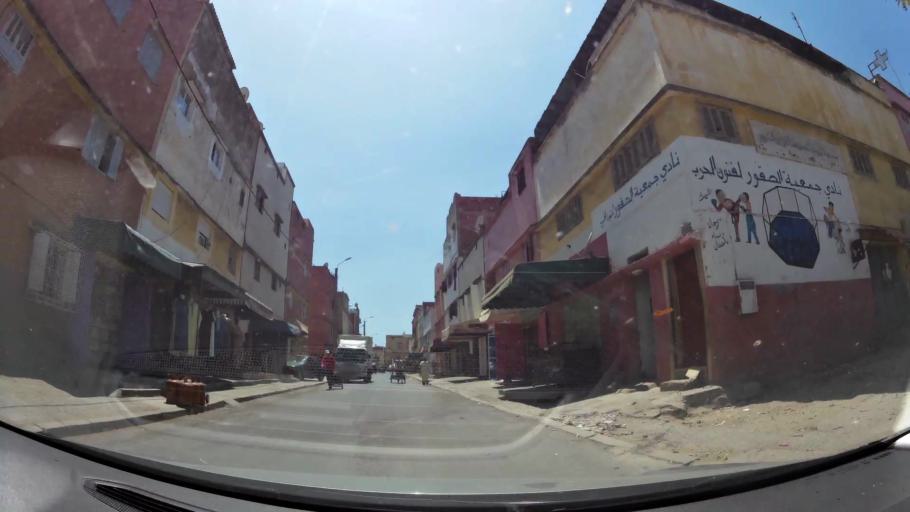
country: MA
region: Gharb-Chrarda-Beni Hssen
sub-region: Kenitra Province
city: Kenitra
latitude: 34.2515
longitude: -6.5467
